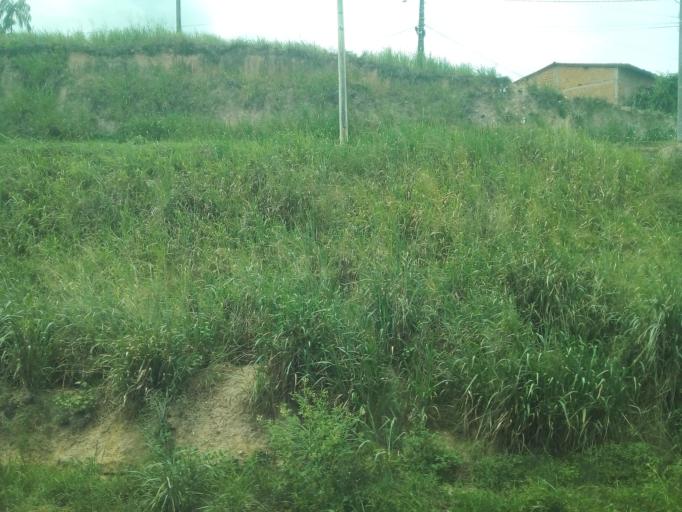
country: BR
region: Maranhao
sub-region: Santa Ines
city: Santa Ines
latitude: -3.6713
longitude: -45.8463
